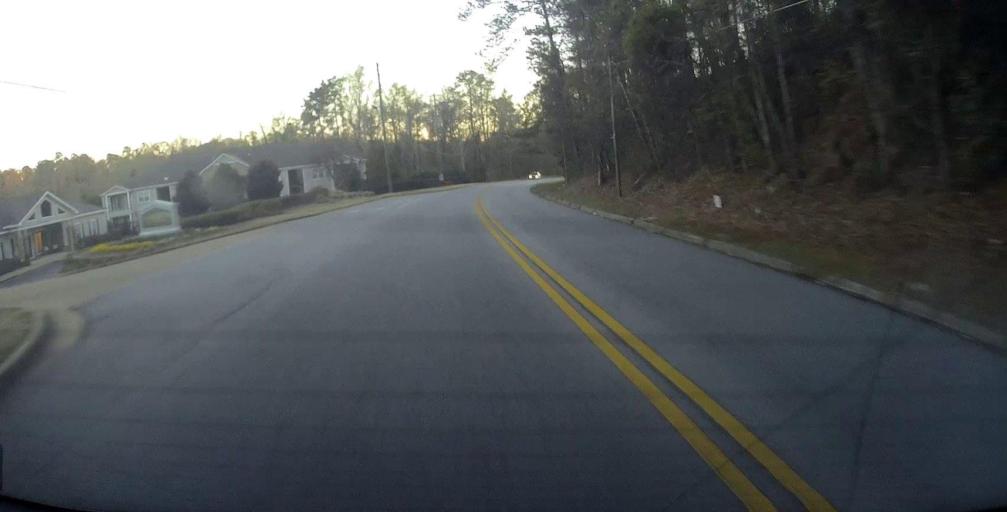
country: US
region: Alabama
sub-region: Russell County
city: Phenix City
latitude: 32.4933
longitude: -85.0182
